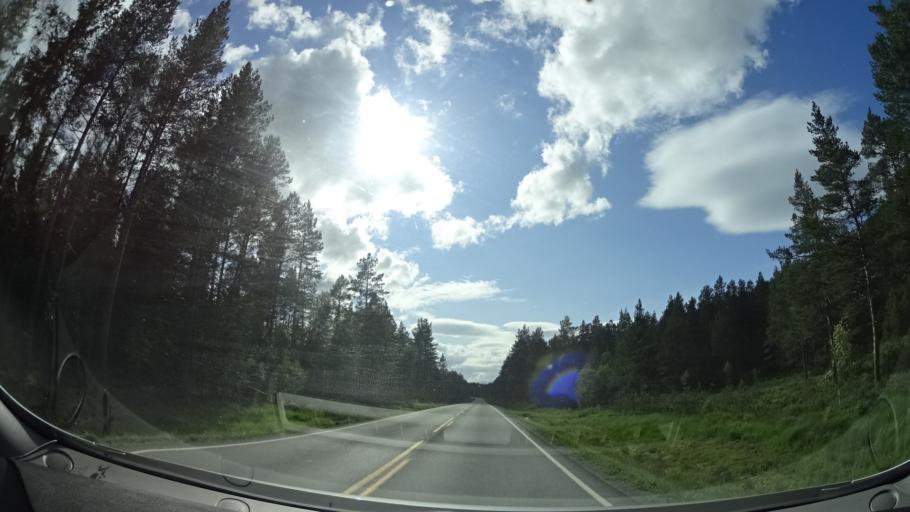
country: NO
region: Sor-Trondelag
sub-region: Hemne
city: Kyrksaeterora
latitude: 63.2112
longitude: 9.0952
